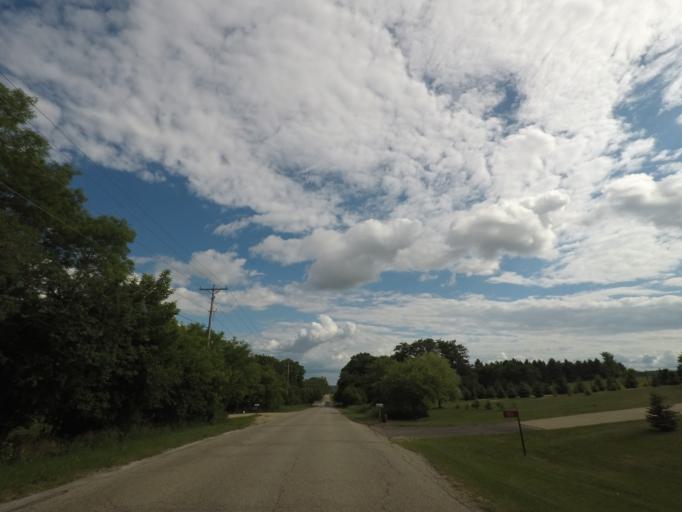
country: US
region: Wisconsin
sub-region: Rock County
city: Janesville
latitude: 42.6918
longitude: -89.0717
